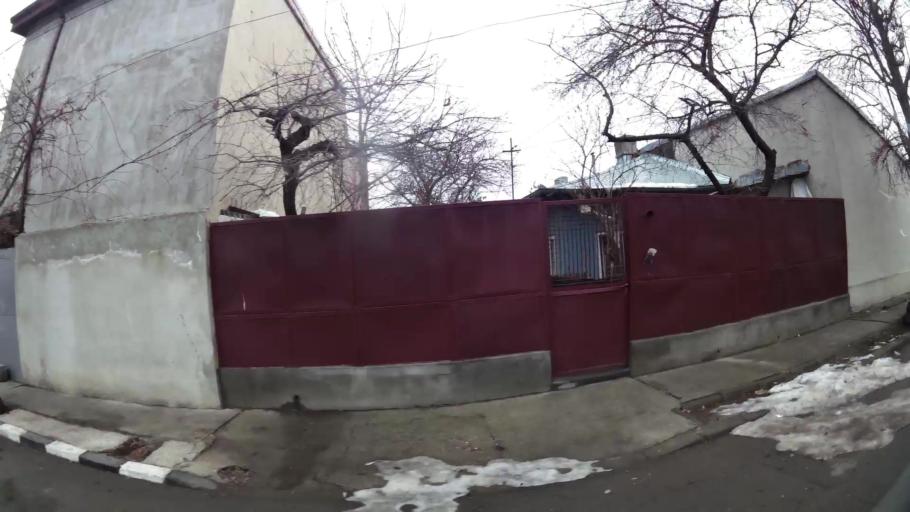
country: RO
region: Ilfov
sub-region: Comuna Chiajna
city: Rosu
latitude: 44.4841
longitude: 26.0189
